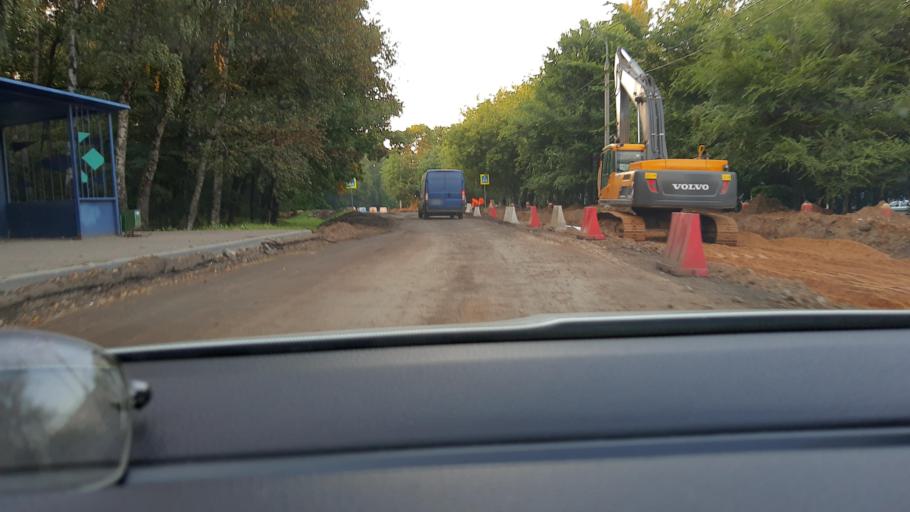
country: RU
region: Moskovskaya
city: Troitsk
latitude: 55.3133
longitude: 37.1749
